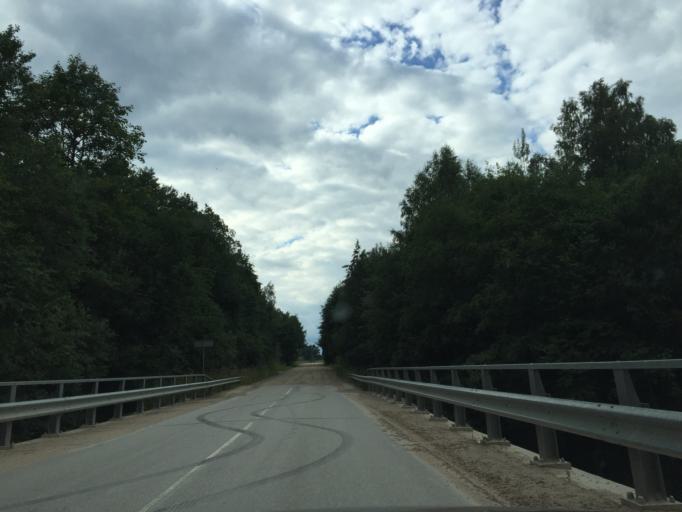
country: LV
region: Malpils
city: Malpils
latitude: 56.9642
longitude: 24.9813
